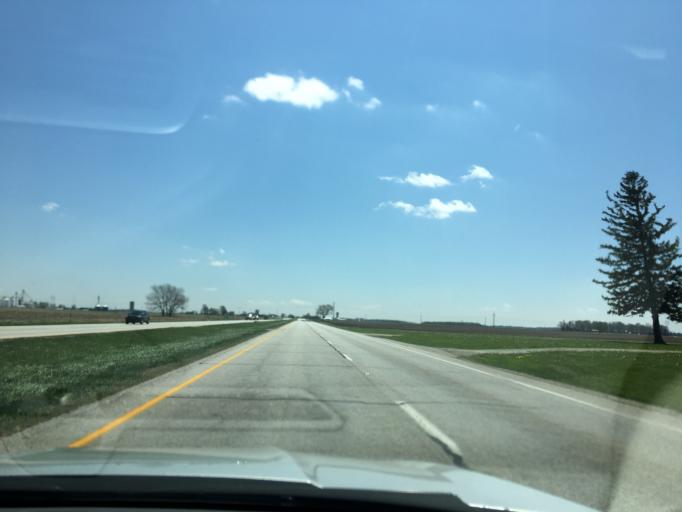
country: US
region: Indiana
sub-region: Clinton County
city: Mulberry
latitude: 40.2509
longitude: -86.6976
